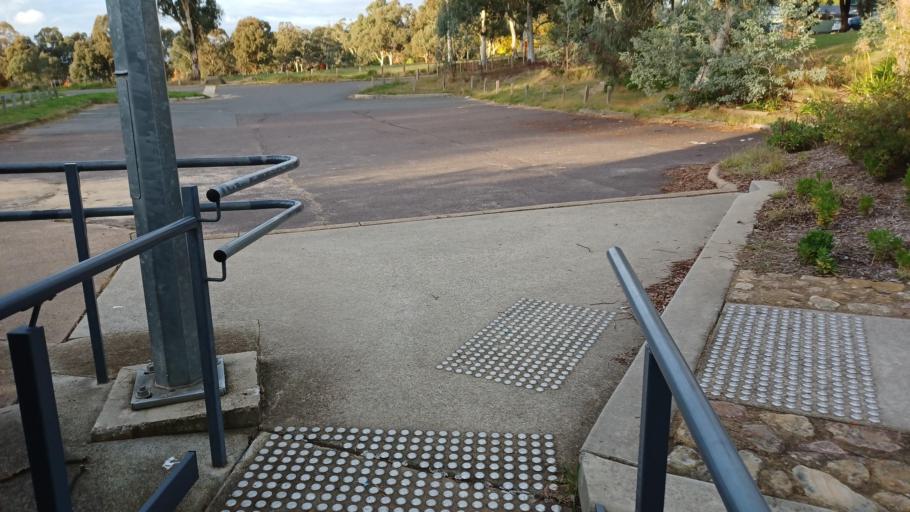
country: AU
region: Australian Capital Territory
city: Belconnen
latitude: -35.1917
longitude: 149.0438
